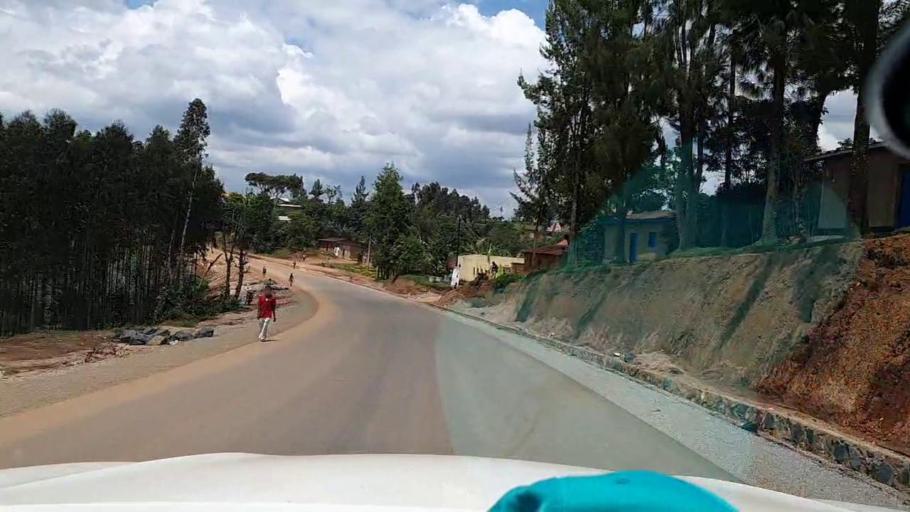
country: RW
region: Southern Province
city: Nzega
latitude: -2.6469
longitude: 29.5667
